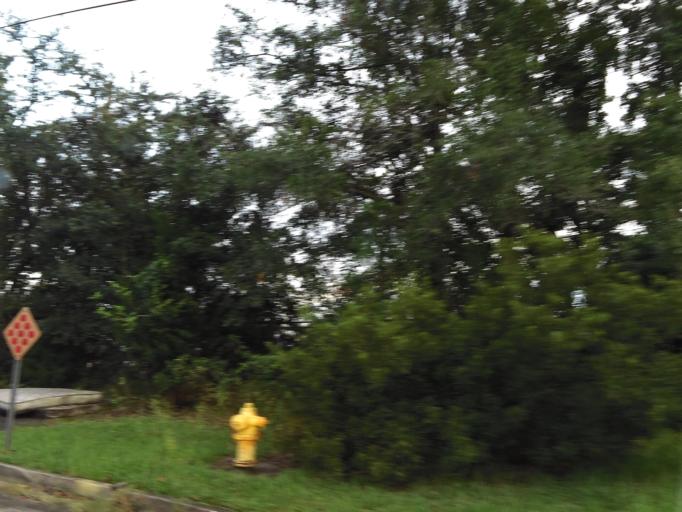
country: US
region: Florida
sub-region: Duval County
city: Jacksonville
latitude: 30.3477
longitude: -81.6986
